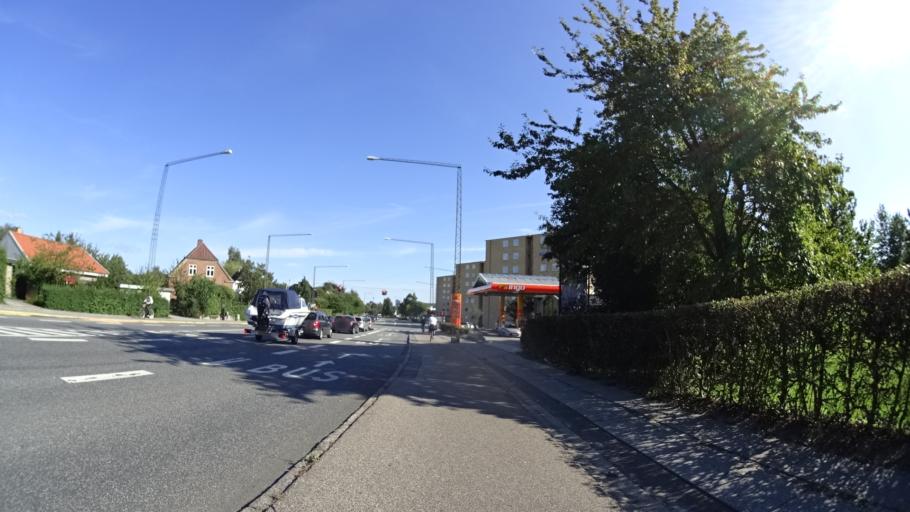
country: DK
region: Central Jutland
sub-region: Arhus Kommune
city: Arhus
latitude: 56.1652
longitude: 10.1681
